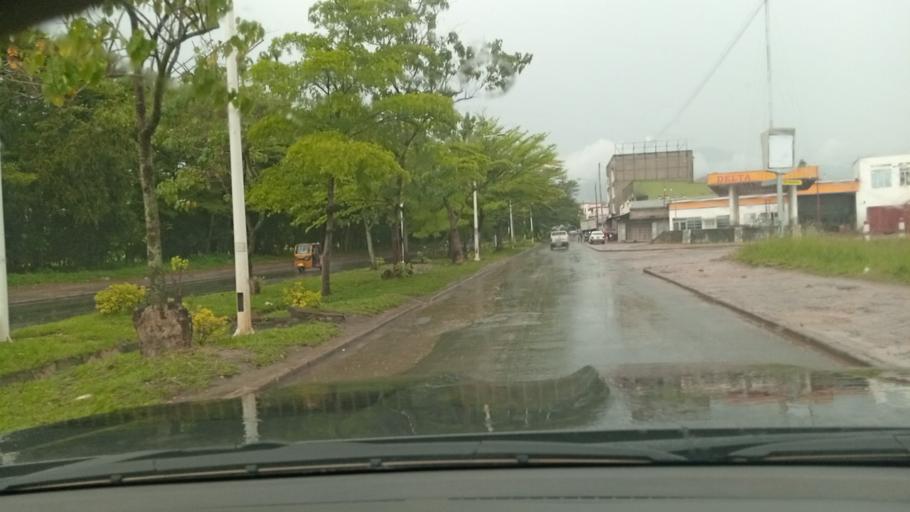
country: BI
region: Bujumbura Mairie
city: Bujumbura
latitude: -3.3796
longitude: 29.3551
